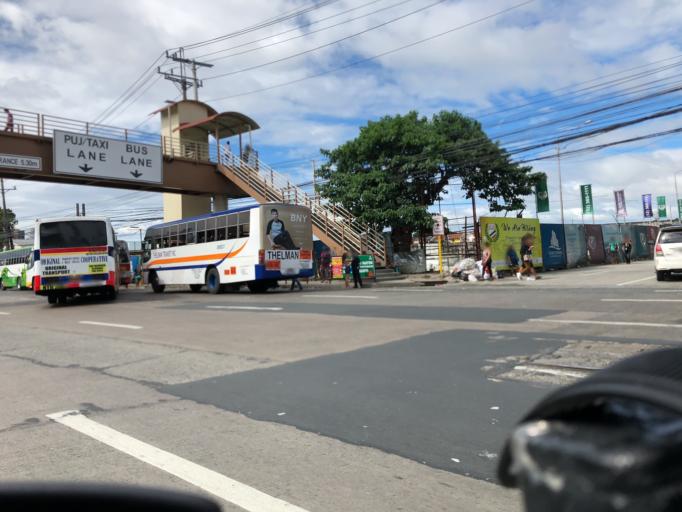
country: PH
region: Calabarzon
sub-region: Province of Rizal
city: San Mateo
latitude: 14.7352
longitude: 121.0591
